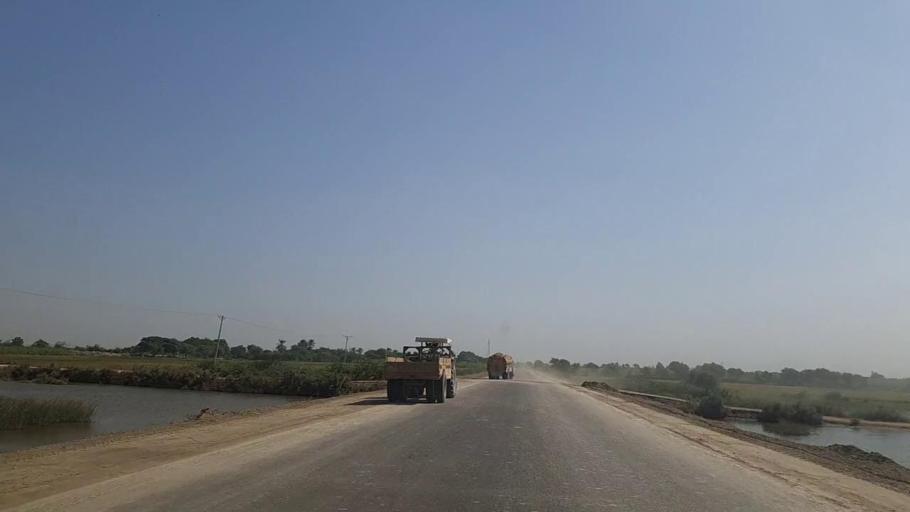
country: PK
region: Sindh
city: Mirpur Batoro
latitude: 24.7464
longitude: 68.2415
